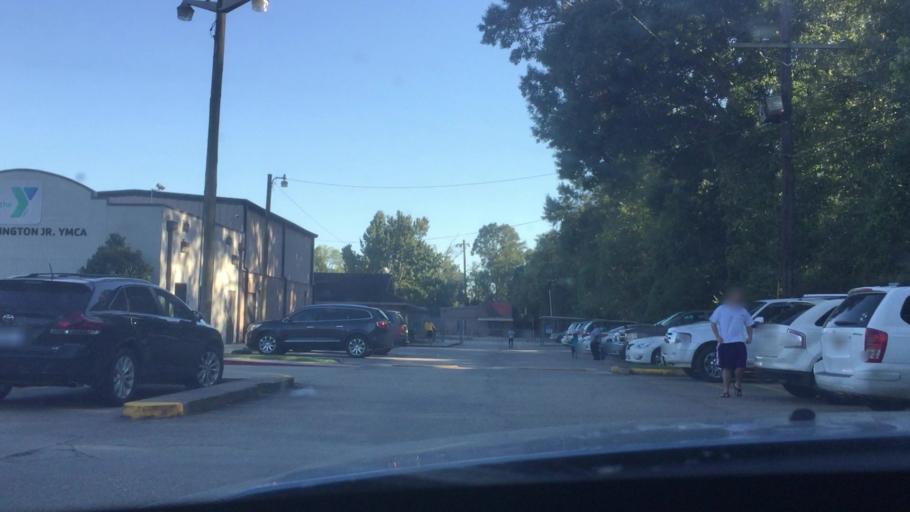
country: US
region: Louisiana
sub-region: East Baton Rouge Parish
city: Monticello
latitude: 30.4577
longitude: -91.0120
